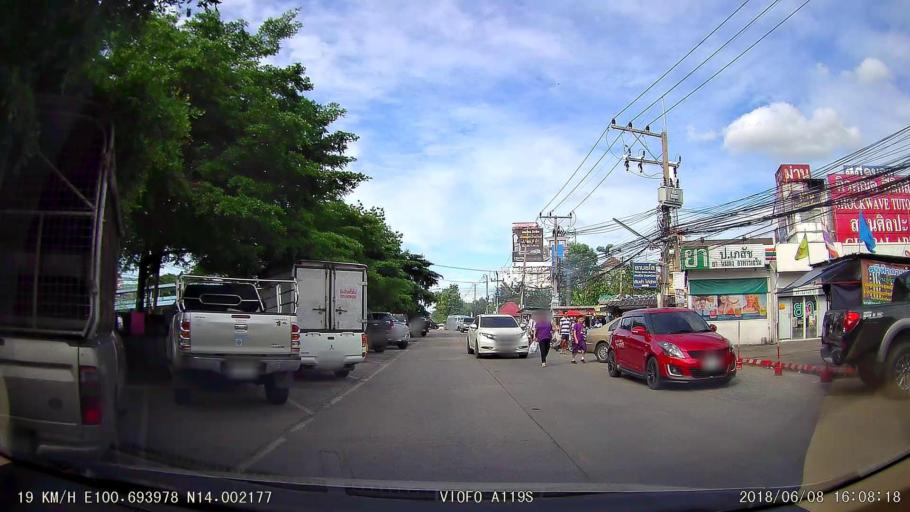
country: TH
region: Pathum Thani
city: Thanyaburi
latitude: 14.0022
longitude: 100.6940
